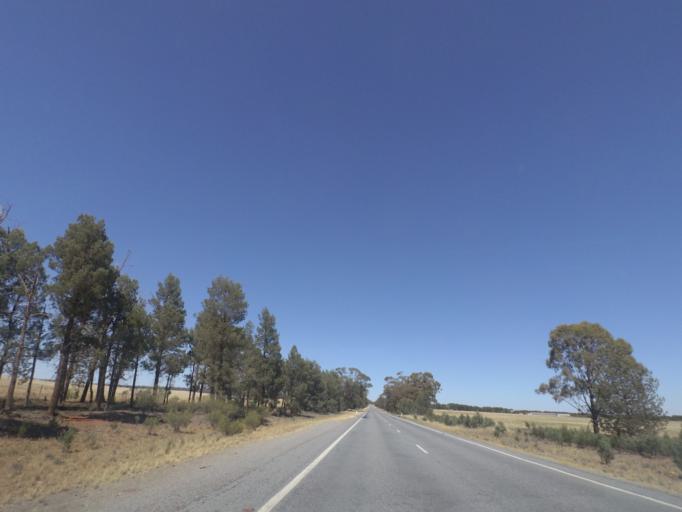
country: AU
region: New South Wales
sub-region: Narrandera
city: Narrandera
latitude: -34.4150
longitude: 146.8624
